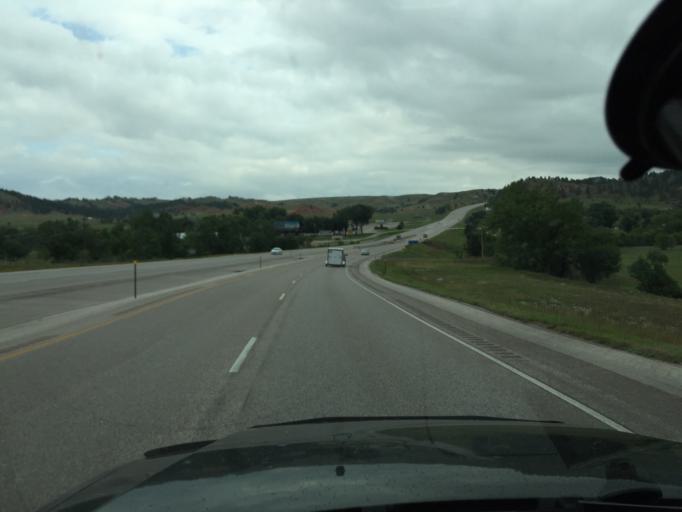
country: US
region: South Dakota
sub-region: Pennington County
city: Colonial Pine Hills
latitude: 43.9858
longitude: -103.2742
